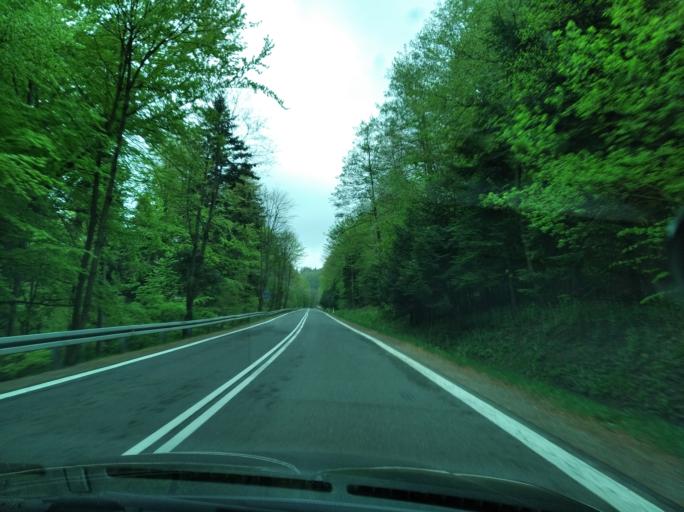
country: PL
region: Subcarpathian Voivodeship
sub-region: Powiat sanocki
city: Tyrawa Woloska
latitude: 49.5622
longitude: 22.3405
